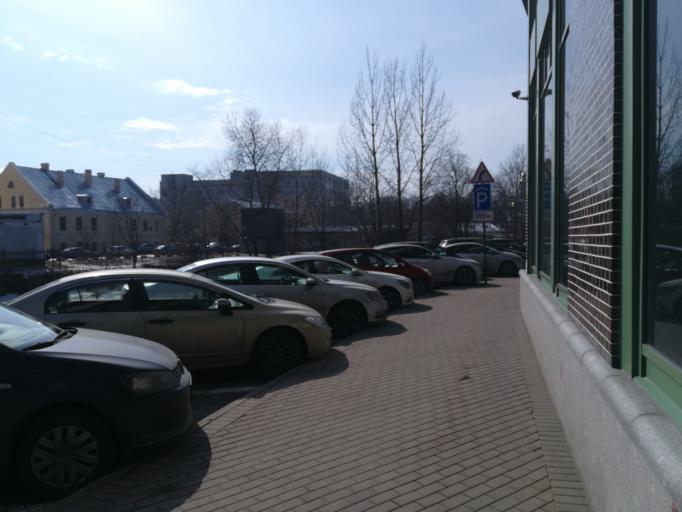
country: RU
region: St.-Petersburg
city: Vasyl'evsky Ostrov
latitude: 59.9472
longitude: 30.2559
